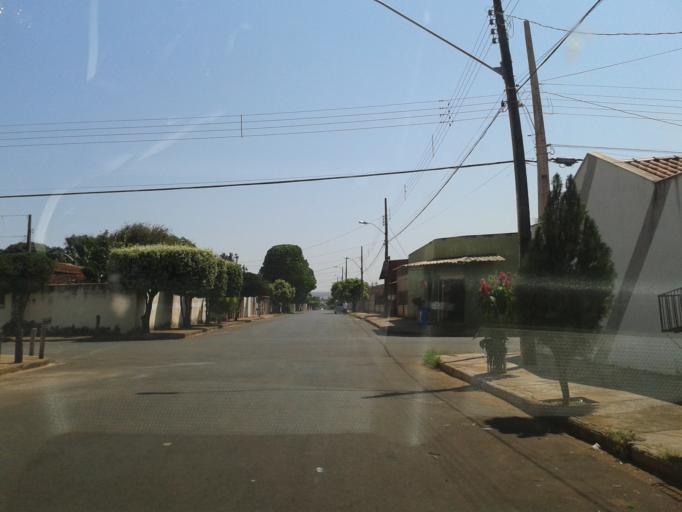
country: BR
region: Minas Gerais
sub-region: Ituiutaba
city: Ituiutaba
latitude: -18.9861
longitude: -49.4468
